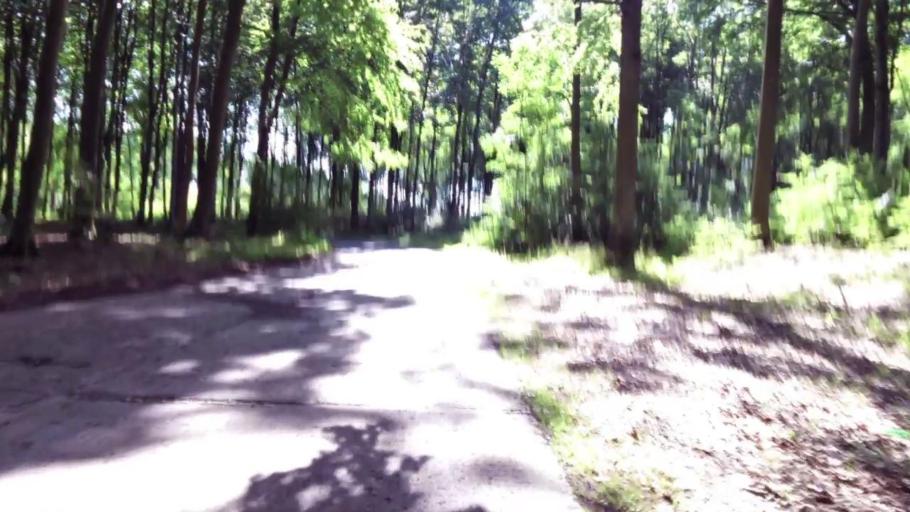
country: PL
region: West Pomeranian Voivodeship
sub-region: Powiat stargardzki
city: Dobrzany
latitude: 53.3891
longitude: 15.4641
